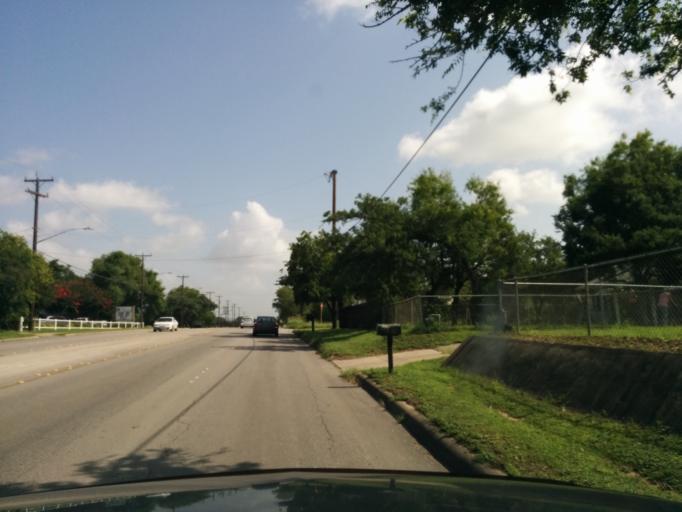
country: US
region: Texas
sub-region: Bexar County
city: Leon Valley
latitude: 29.5477
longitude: -98.6149
